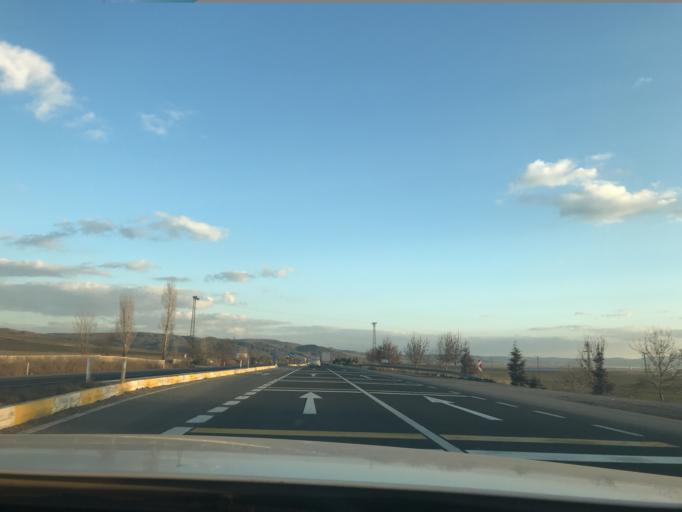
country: TR
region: Ankara
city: Altpinar
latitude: 39.3821
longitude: 32.8926
